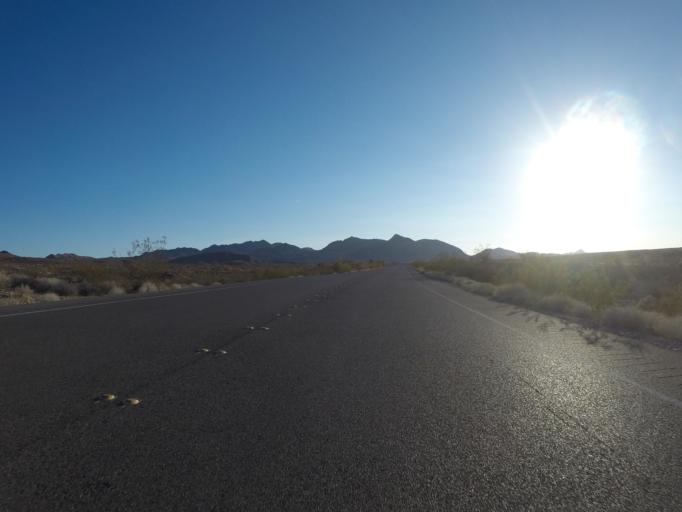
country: US
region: Nevada
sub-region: Clark County
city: Moapa Valley
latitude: 36.2877
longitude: -114.4882
